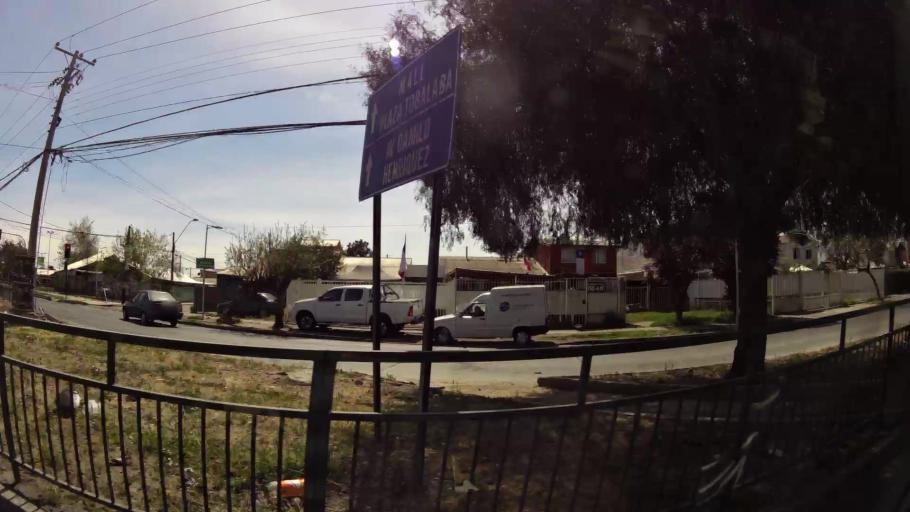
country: CL
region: Santiago Metropolitan
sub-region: Provincia de Cordillera
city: Puente Alto
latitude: -33.5772
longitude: -70.5749
